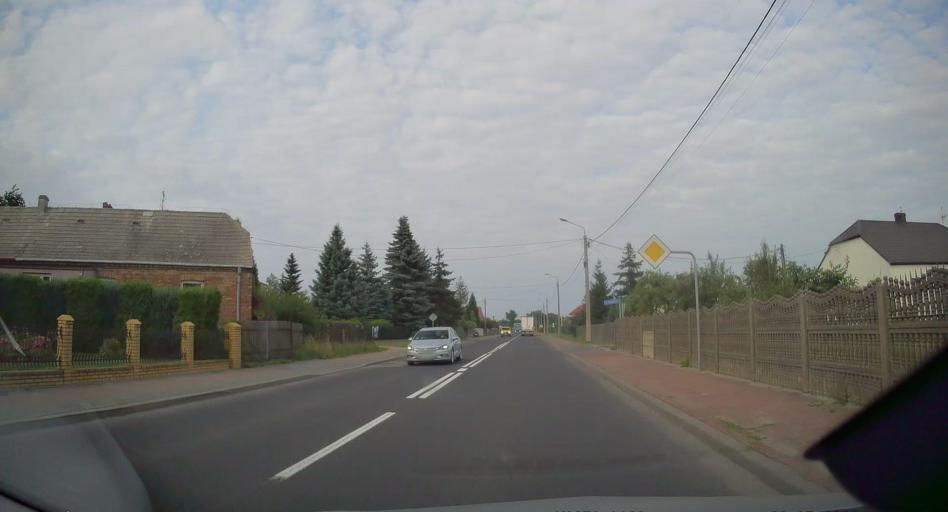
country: PL
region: Silesian Voivodeship
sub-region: Powiat czestochowski
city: Klomnice
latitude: 50.9237
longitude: 19.3634
